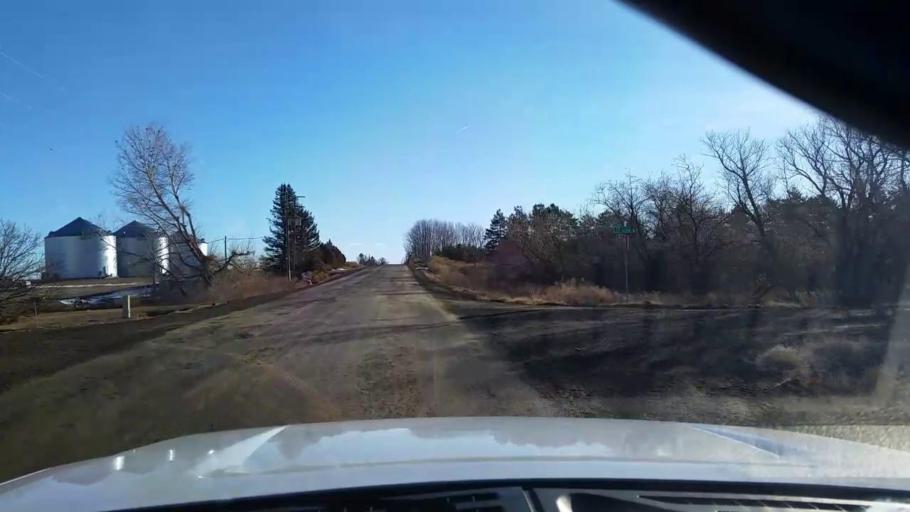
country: US
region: Colorado
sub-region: Larimer County
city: Wellington
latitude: 40.7696
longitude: -105.0955
